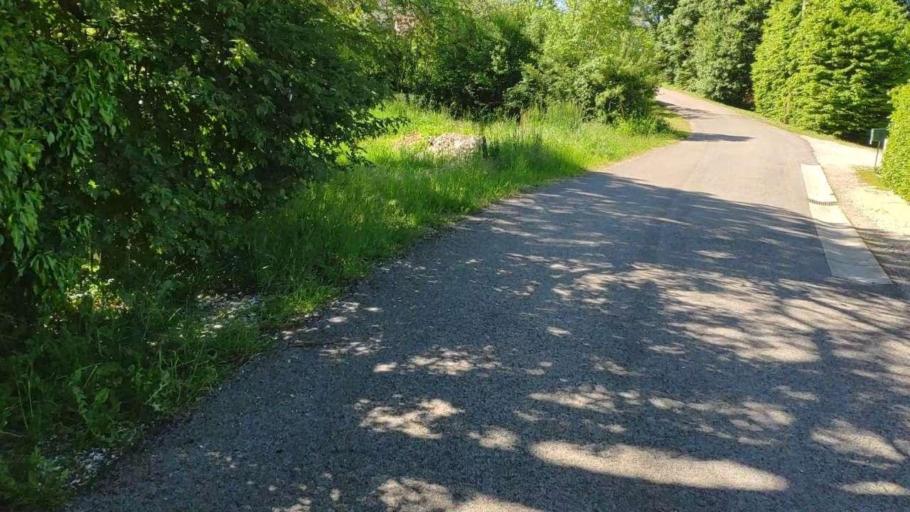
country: FR
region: Franche-Comte
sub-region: Departement du Jura
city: Clairvaux-les-Lacs
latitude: 46.6982
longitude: 5.7250
